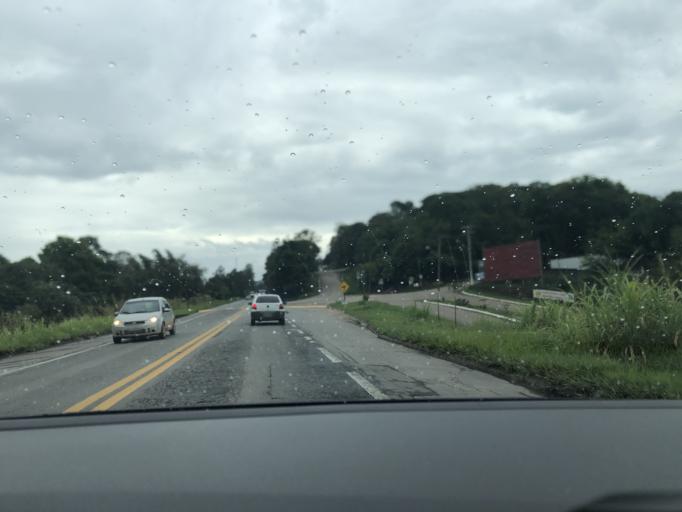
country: BR
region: Sao Paulo
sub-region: Campo Limpo Paulista
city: Campo Limpo Paulista
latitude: -23.1617
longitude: -46.7538
